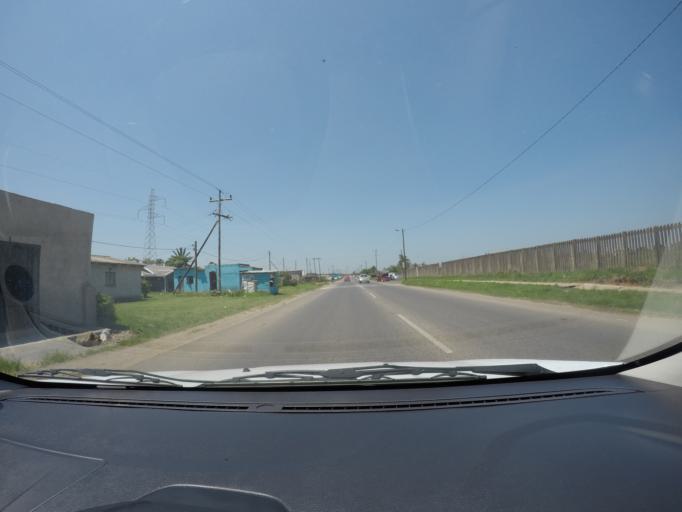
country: ZA
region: KwaZulu-Natal
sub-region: uThungulu District Municipality
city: eSikhawini
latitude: -28.8639
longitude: 31.9113
